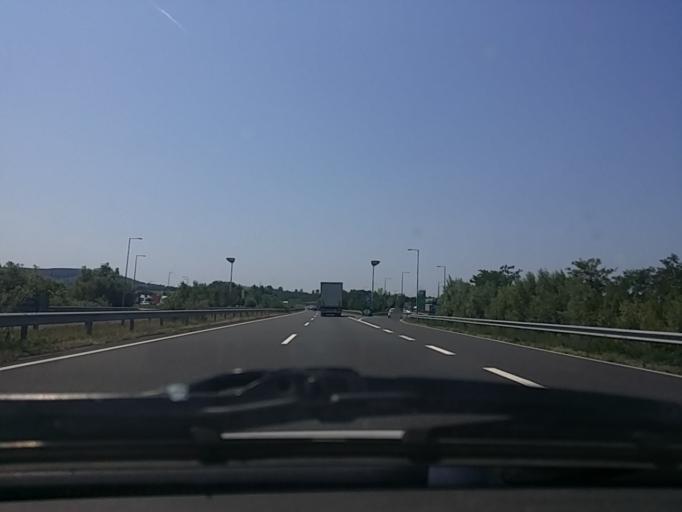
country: HU
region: Somogy
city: Balatonlelle
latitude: 46.7786
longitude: 17.7231
